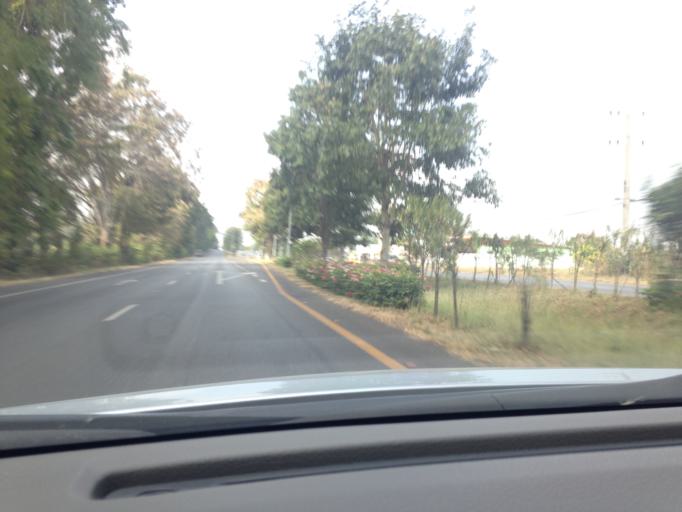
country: TH
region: Phetchabun
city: Wichian Buri
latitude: 15.6743
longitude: 101.0327
